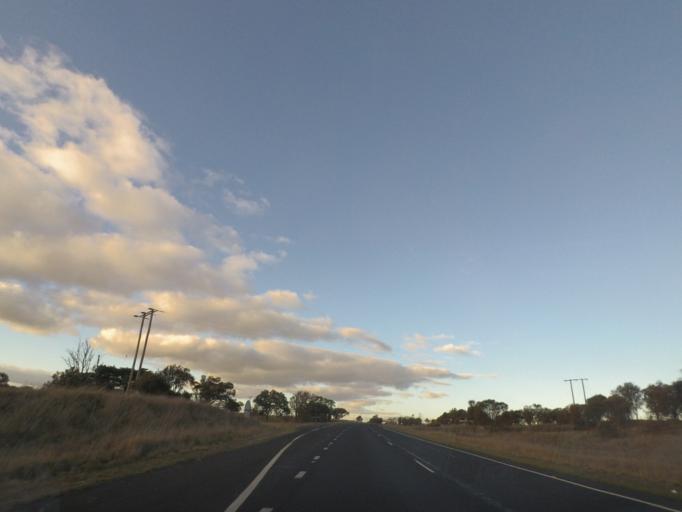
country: AU
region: New South Wales
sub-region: Yass Valley
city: Yass
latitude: -34.7679
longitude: 148.7519
